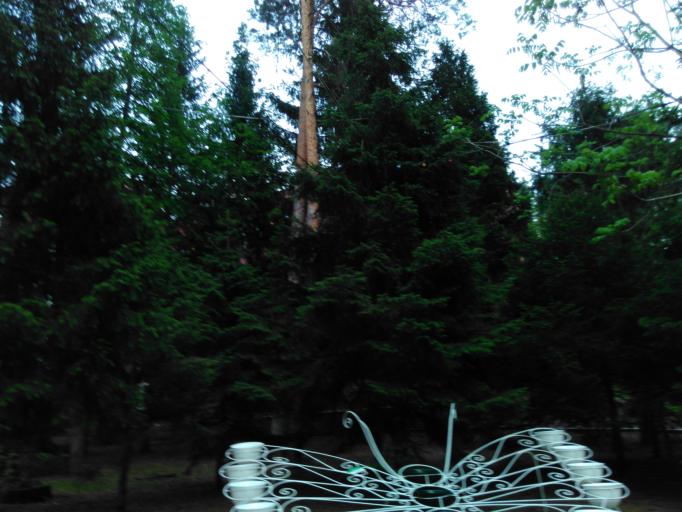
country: RU
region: Tatarstan
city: Al'met'yevsk
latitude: 54.9517
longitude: 52.2648
